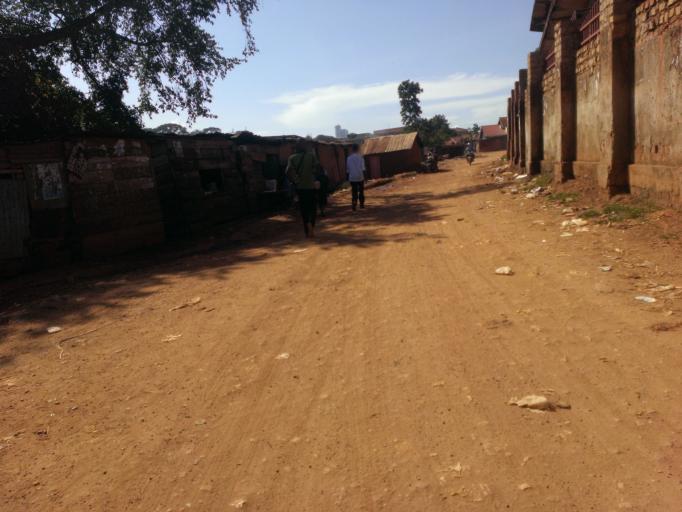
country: UG
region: Central Region
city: Kampala Central Division
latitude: 0.3282
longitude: 32.5612
